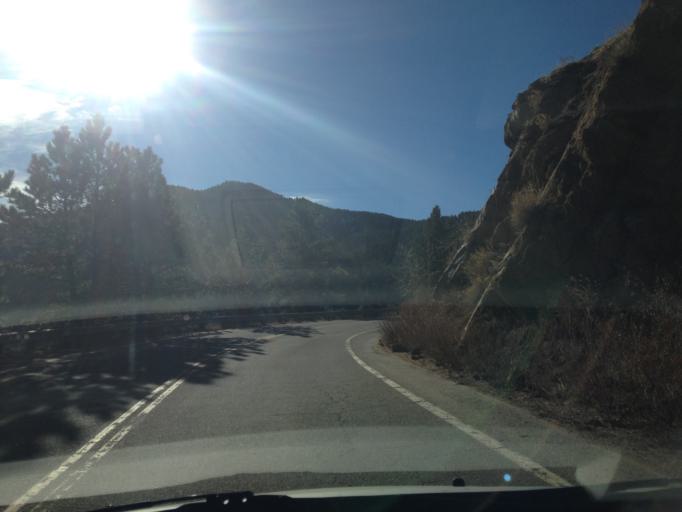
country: US
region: Colorado
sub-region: Boulder County
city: Boulder
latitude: 40.0010
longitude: -105.2987
